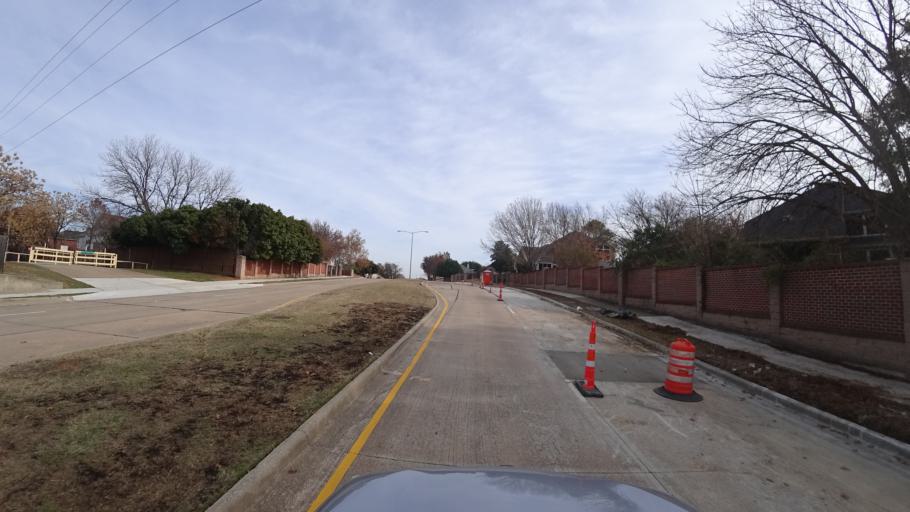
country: US
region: Texas
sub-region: Denton County
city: Highland Village
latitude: 33.0831
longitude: -97.0313
